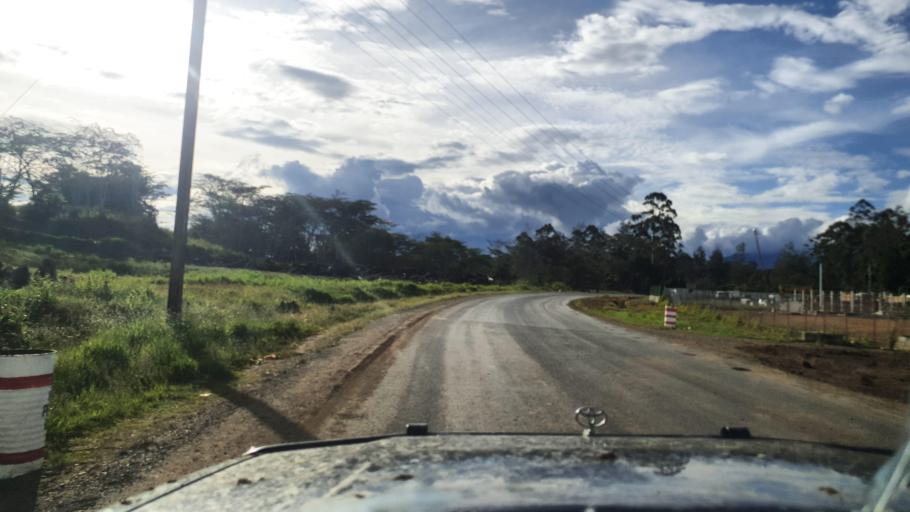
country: PG
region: Jiwaka
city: Minj
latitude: -5.8486
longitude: 144.6232
